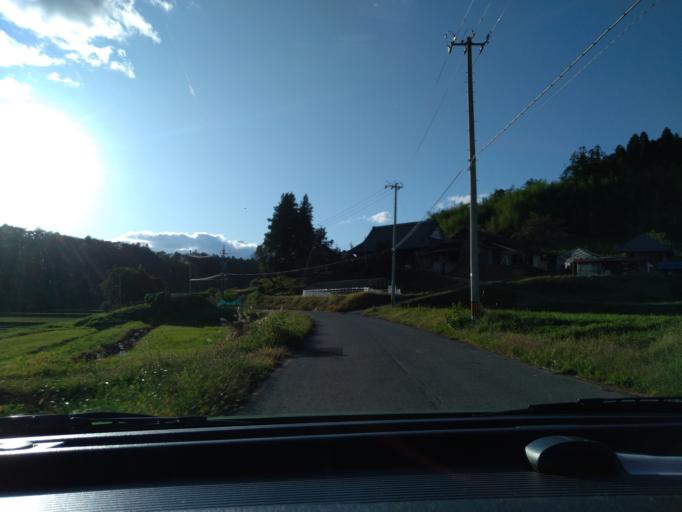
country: JP
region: Iwate
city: Ichinoseki
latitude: 38.8682
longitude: 141.1848
